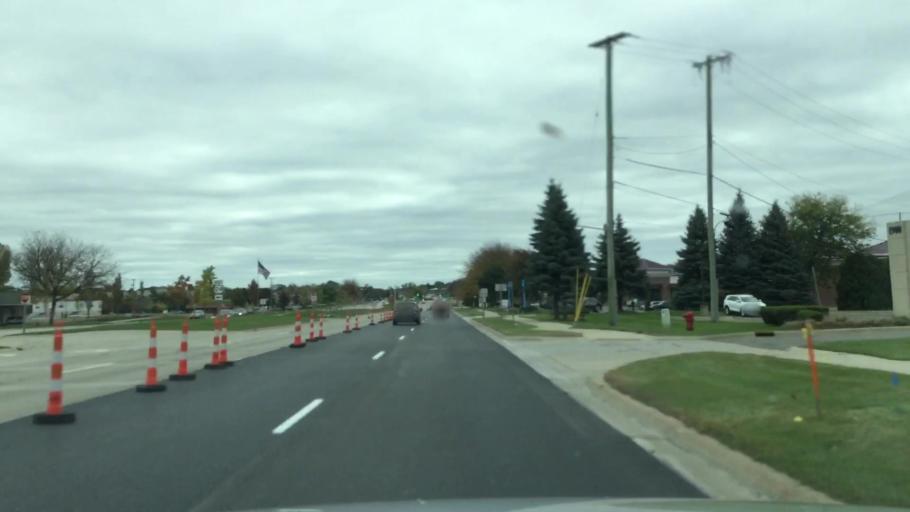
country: US
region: Michigan
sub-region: Oakland County
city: Sylvan Lake
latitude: 42.6113
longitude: -83.3054
